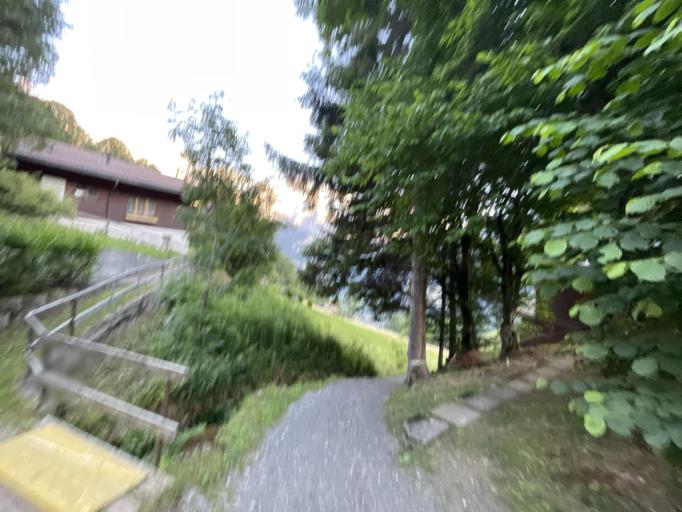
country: CH
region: Bern
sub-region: Interlaken-Oberhasli District
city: Lauterbrunnen
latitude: 46.6113
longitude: 7.9118
